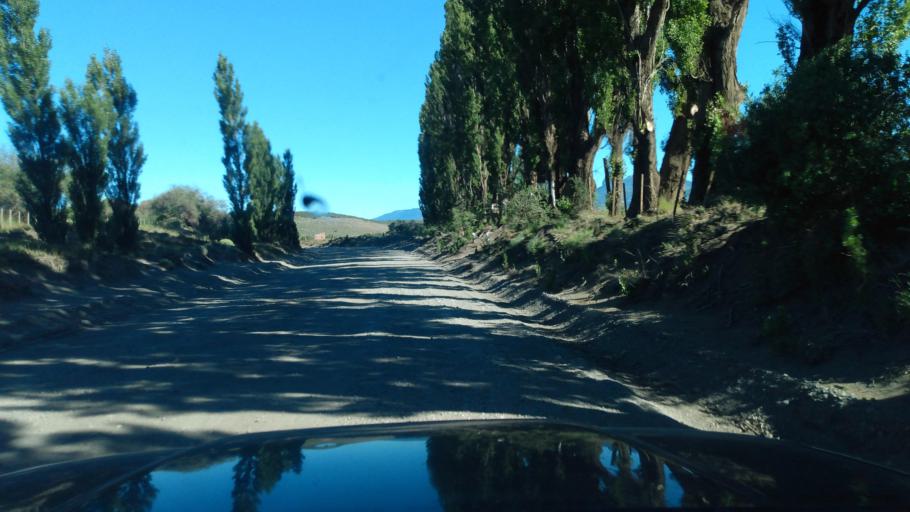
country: AR
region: Neuquen
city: Junin de los Andes
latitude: -39.8298
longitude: -71.1926
